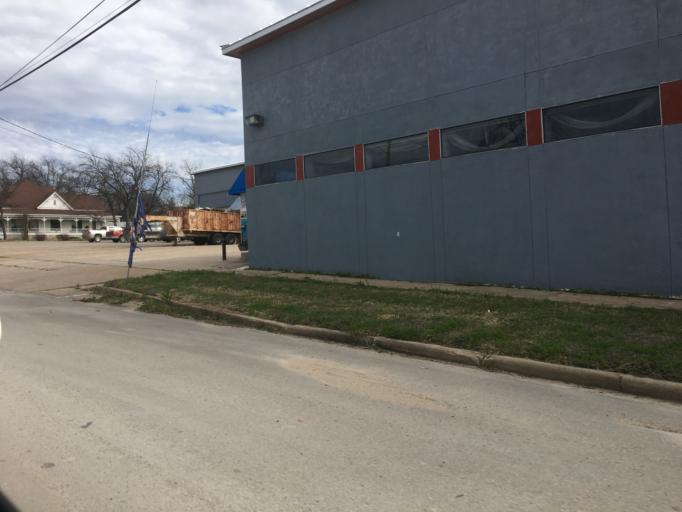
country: US
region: Texas
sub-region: Erath County
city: Dublin
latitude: 32.0863
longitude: -98.3420
